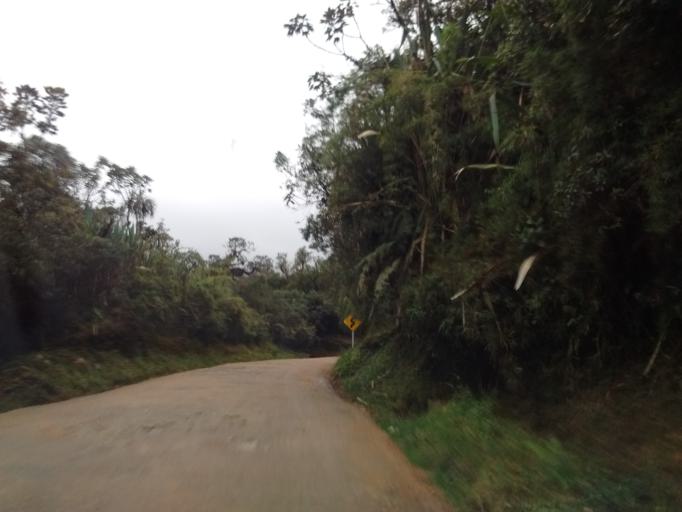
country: CO
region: Huila
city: Isnos
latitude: 2.1297
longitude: -76.3801
